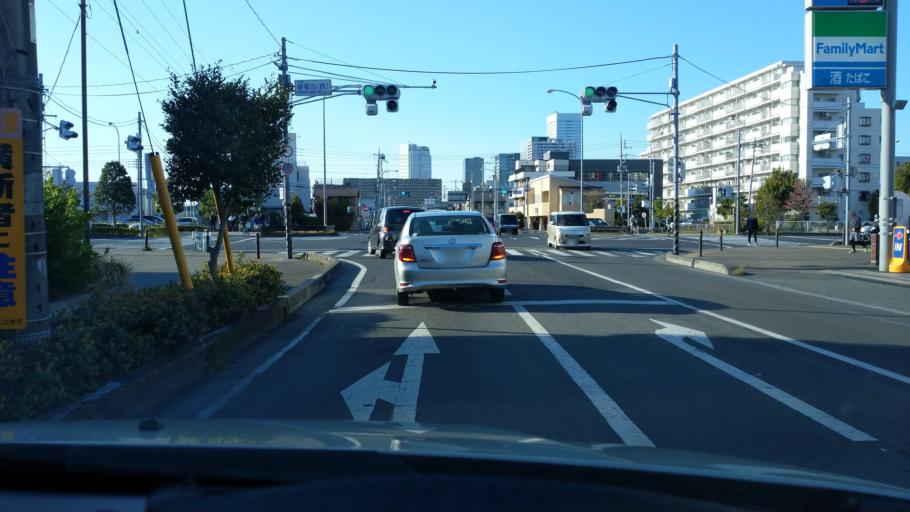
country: JP
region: Saitama
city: Yono
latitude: 35.8966
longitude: 139.6213
